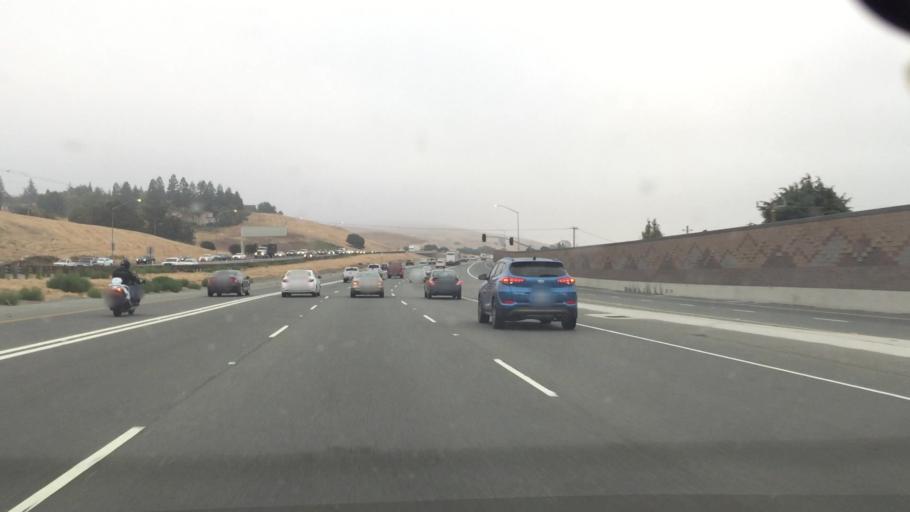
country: US
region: California
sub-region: Santa Clara County
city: Milpitas
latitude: 37.4937
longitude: -121.9215
